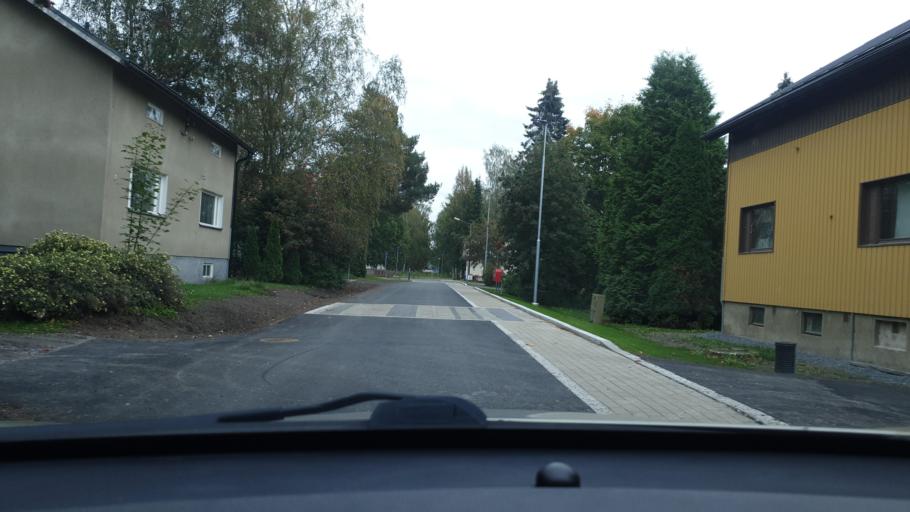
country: FI
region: Ostrobothnia
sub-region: Vaasa
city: Korsholm
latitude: 63.0948
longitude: 21.6751
